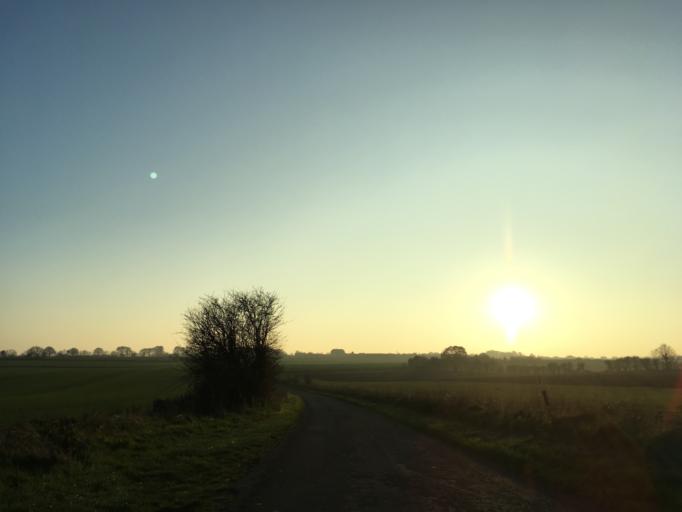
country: GB
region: England
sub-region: South Gloucestershire
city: Marshfield
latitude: 51.4726
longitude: -2.2957
